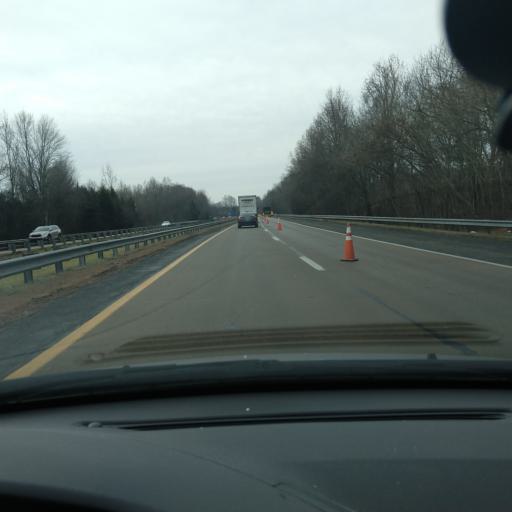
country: US
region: North Carolina
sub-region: Forsyth County
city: Winston-Salem
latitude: 36.0273
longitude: -80.2366
